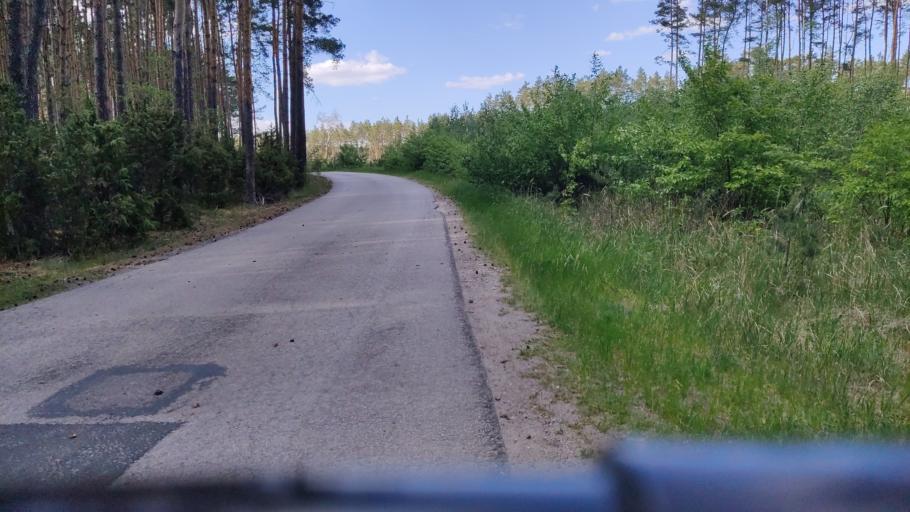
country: PL
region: Kujawsko-Pomorskie
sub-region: Wloclawek
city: Wloclawek
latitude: 52.5976
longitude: 19.0833
